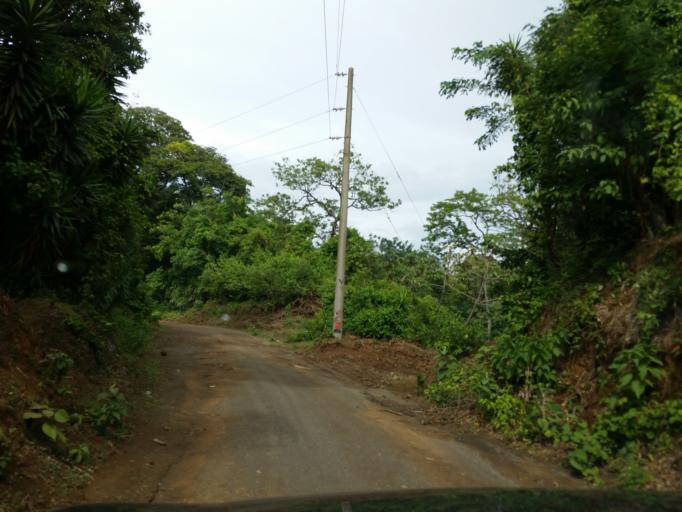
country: NI
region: Managua
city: El Crucero
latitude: 12.0124
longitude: -86.3327
